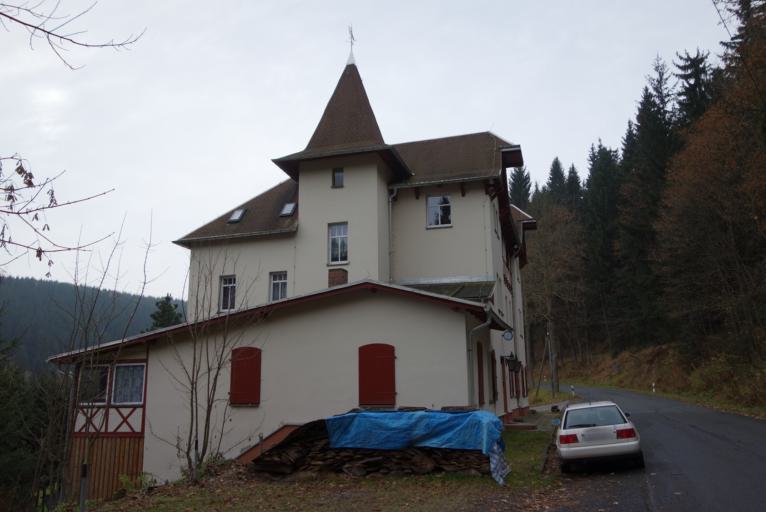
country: DE
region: Saxony
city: Olbernhau
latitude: 50.6083
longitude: 13.3233
